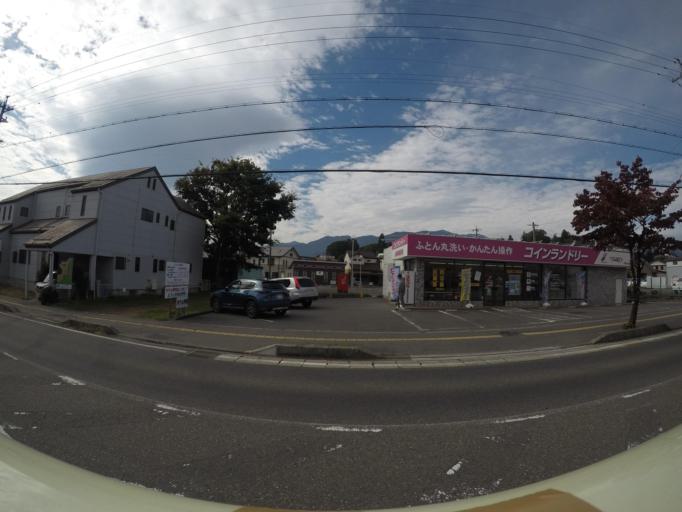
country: JP
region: Nagano
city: Ina
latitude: 35.8412
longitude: 137.9571
